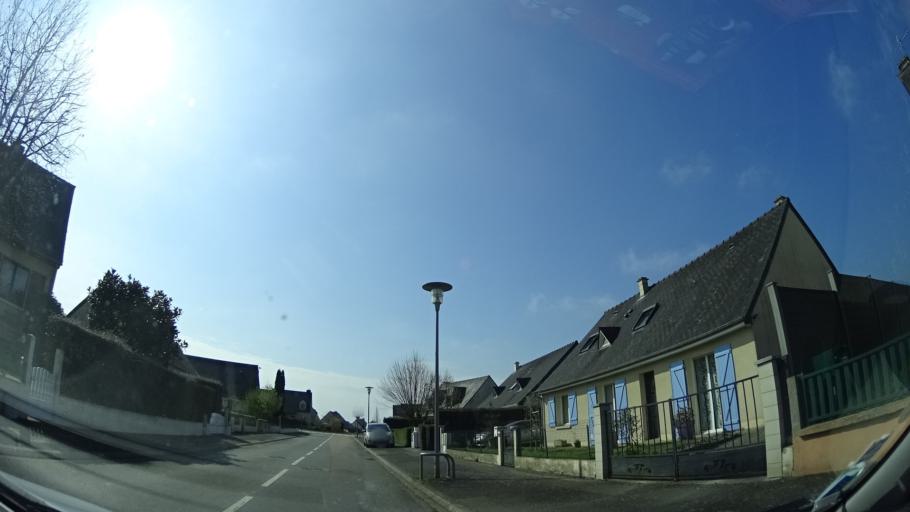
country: FR
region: Brittany
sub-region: Departement d'Ille-et-Vilaine
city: Bedee
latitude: 48.1797
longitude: -1.9509
